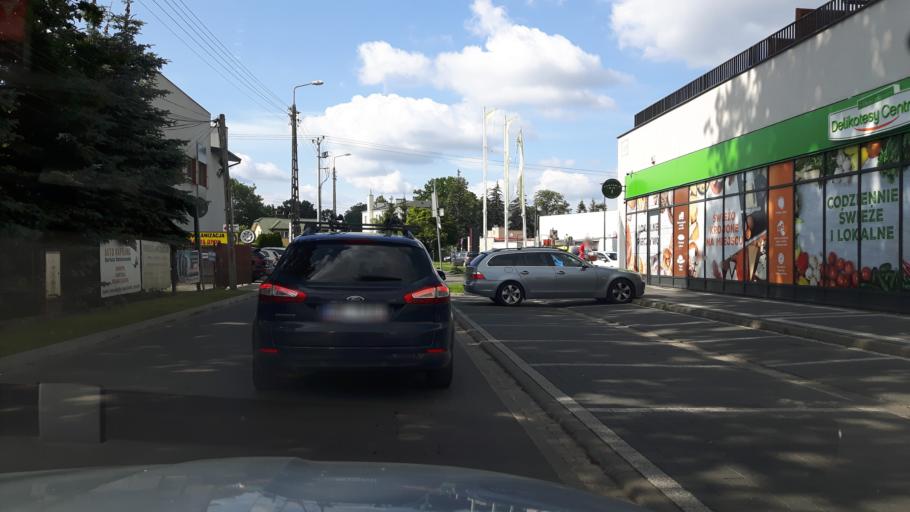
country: PL
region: Masovian Voivodeship
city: Zielonka
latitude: 52.3013
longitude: 21.1576
